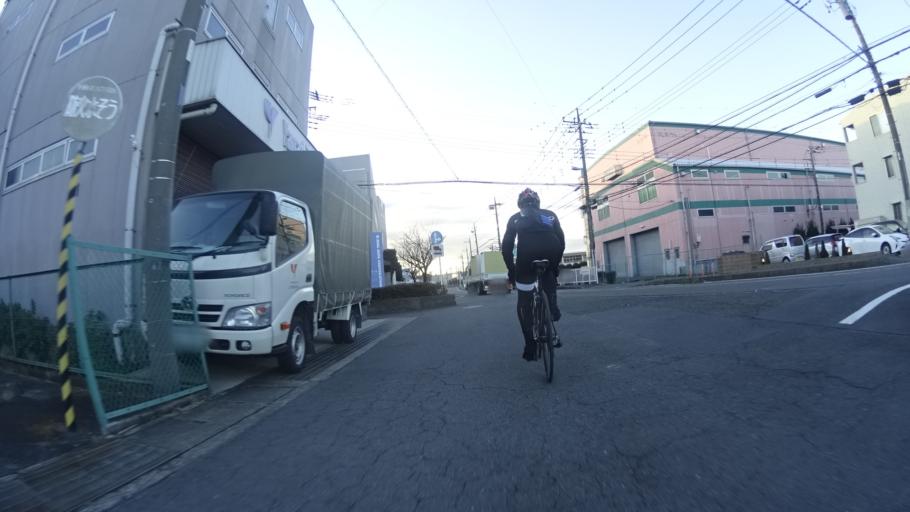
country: JP
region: Kanagawa
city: Atsugi
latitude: 35.4594
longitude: 139.3681
